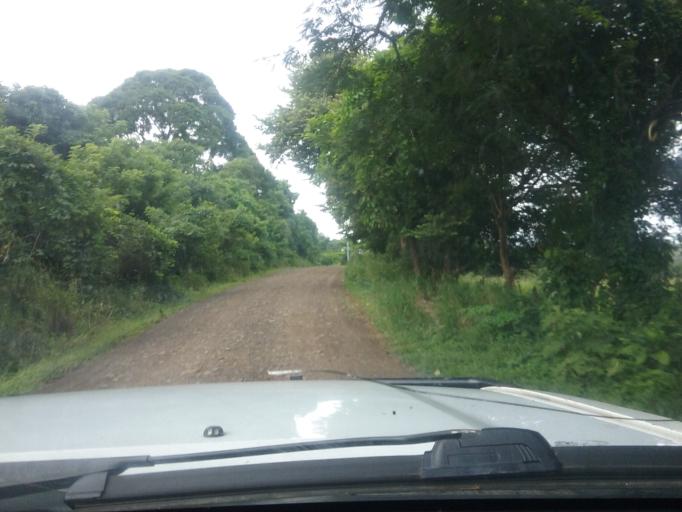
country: NI
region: Matagalpa
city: Matagalpa
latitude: 12.8786
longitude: -85.9593
